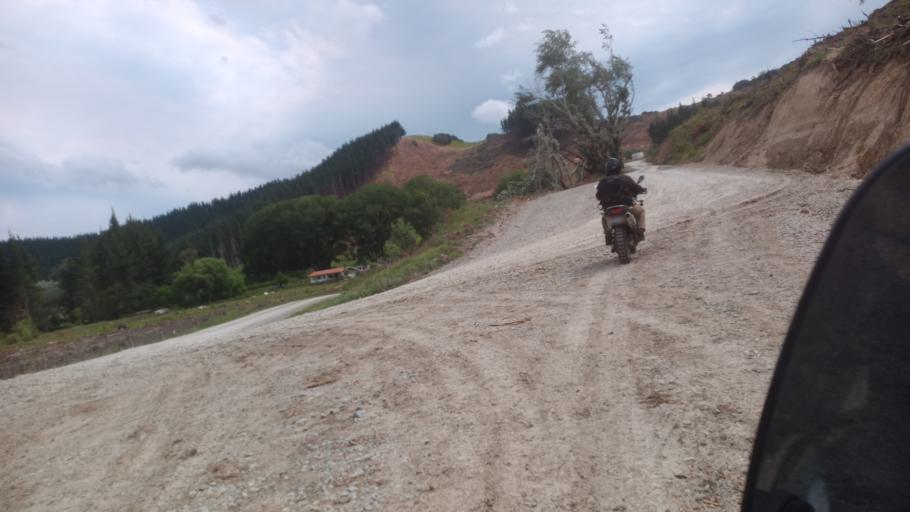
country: NZ
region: Gisborne
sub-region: Gisborne District
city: Gisborne
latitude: -38.4632
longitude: 177.9051
